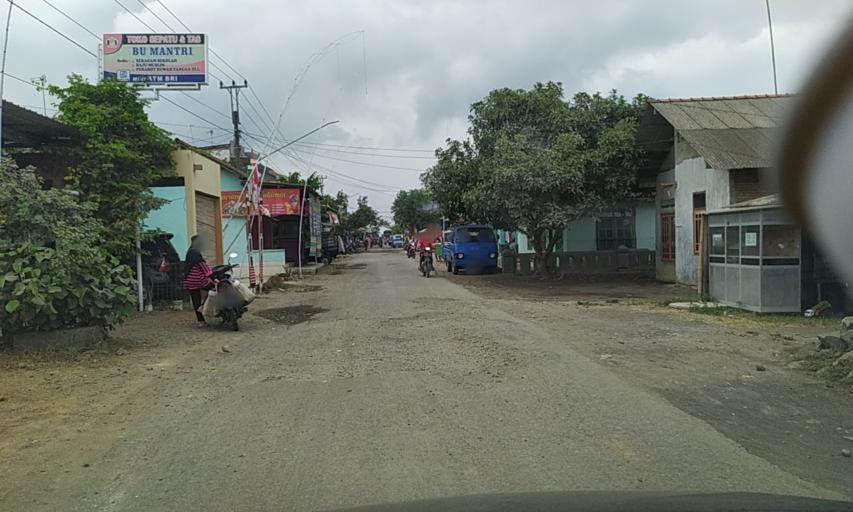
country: ID
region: Central Java
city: Jeruklegi
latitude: -7.6450
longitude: 108.9508
